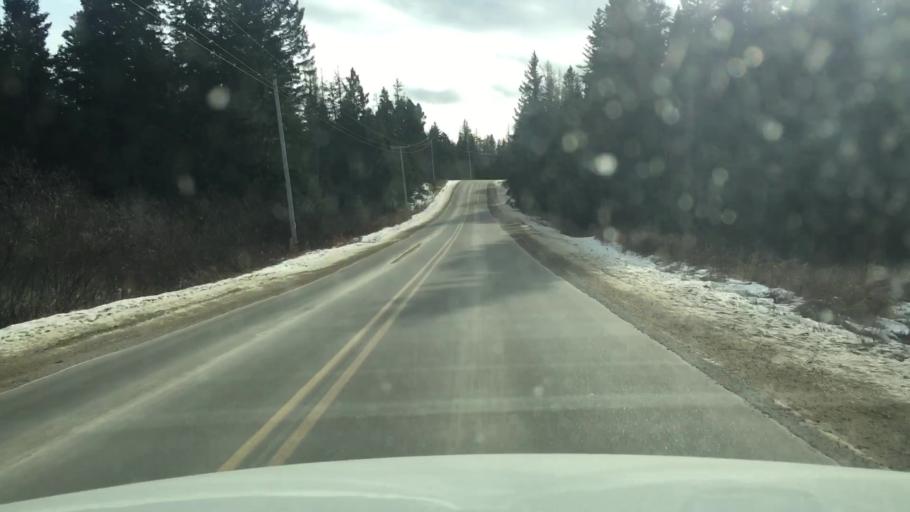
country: US
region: Maine
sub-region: Washington County
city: Jonesport
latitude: 44.6355
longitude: -67.5933
